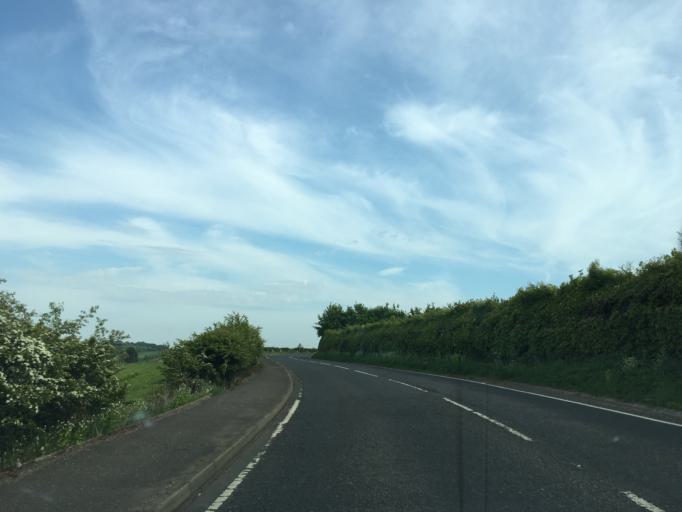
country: GB
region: Scotland
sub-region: Midlothian
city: Loanhead
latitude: 55.8832
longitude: -3.1964
